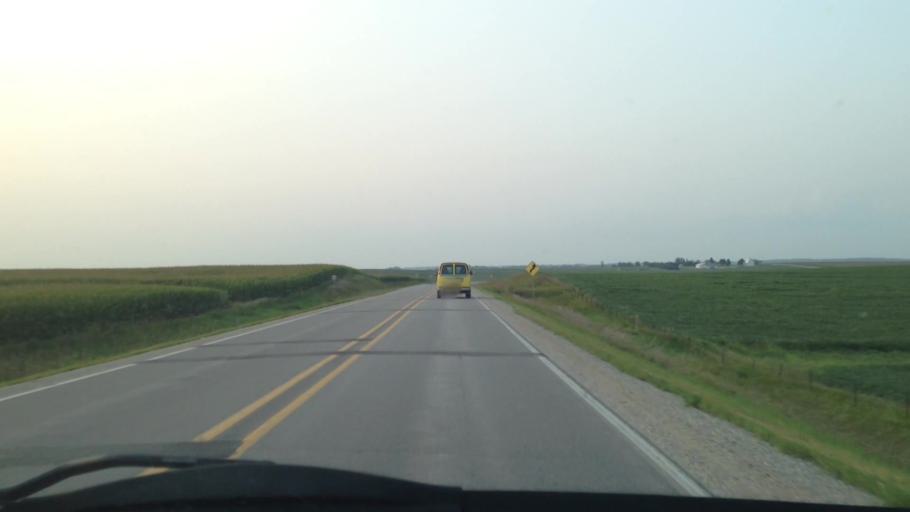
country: US
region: Iowa
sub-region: Benton County
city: Atkins
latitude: 42.0316
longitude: -91.8742
